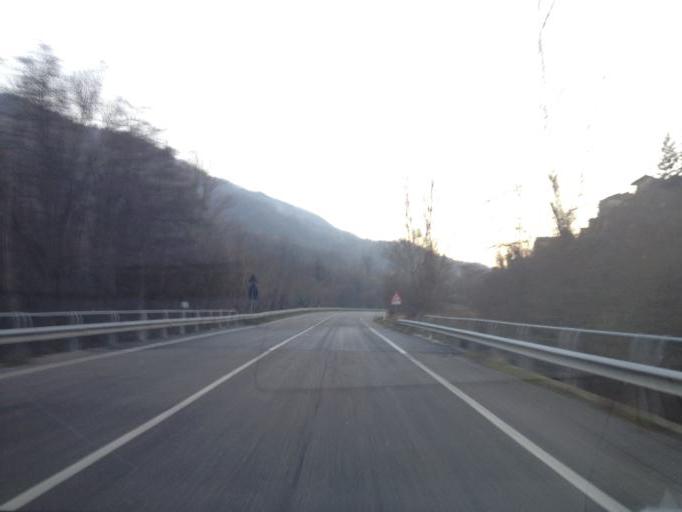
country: IT
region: The Marches
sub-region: Provincia di Ascoli Piceno
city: Arquata del Tronto
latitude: 42.7612
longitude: 13.2854
